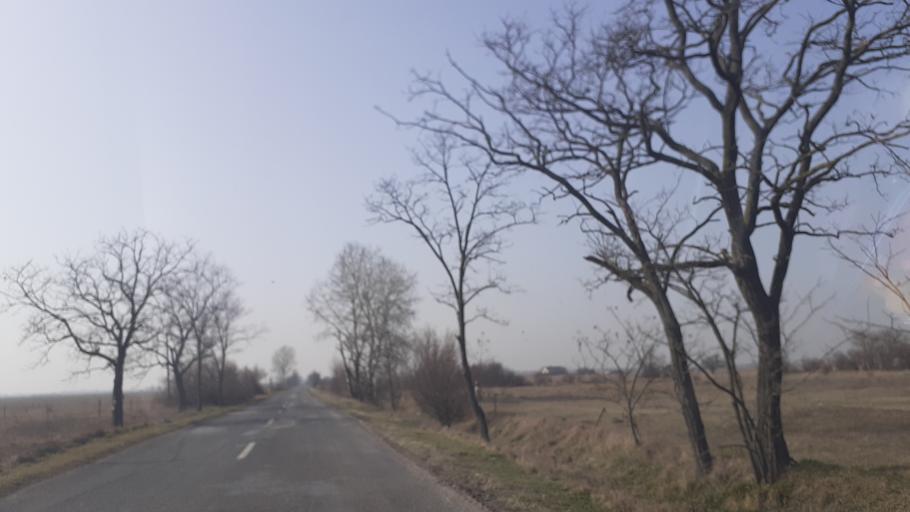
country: HU
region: Bacs-Kiskun
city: Kunszentmiklos
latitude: 47.0234
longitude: 19.1750
